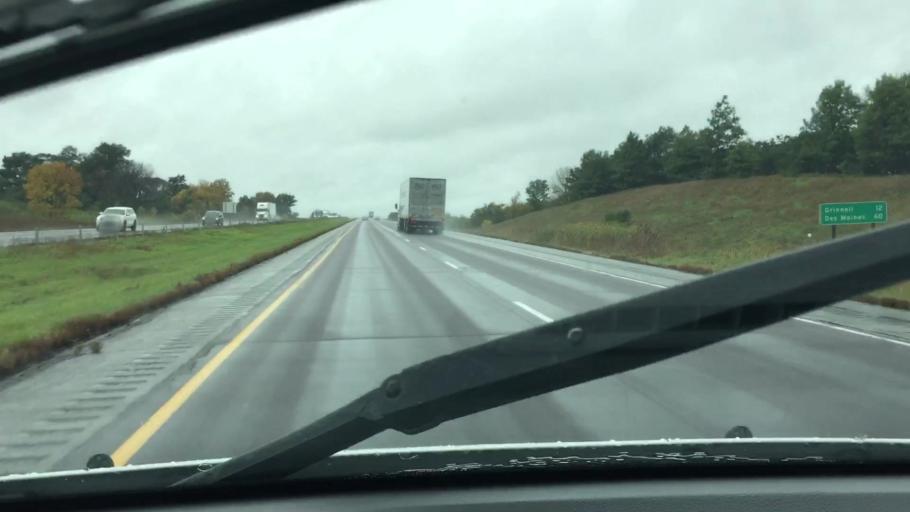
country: US
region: Iowa
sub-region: Poweshiek County
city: Montezuma
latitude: 41.6964
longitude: -92.5686
